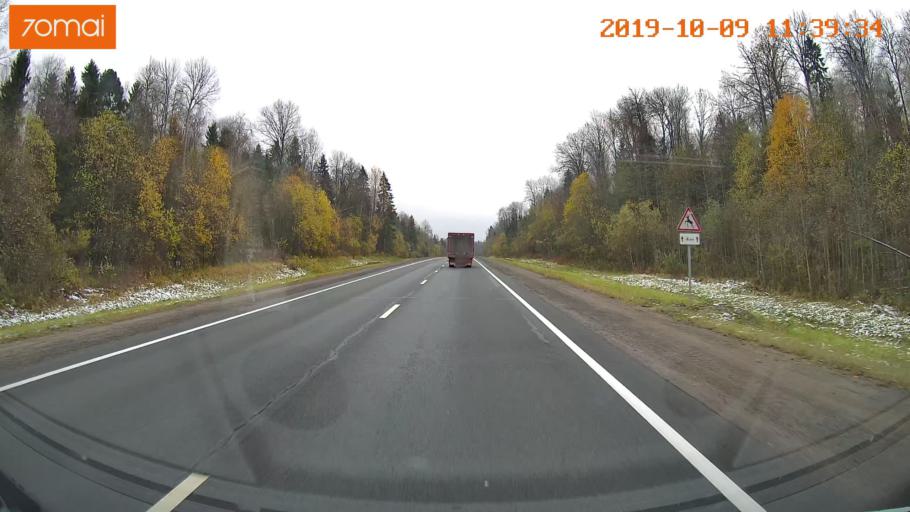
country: RU
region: Vologda
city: Gryazovets
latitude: 58.9545
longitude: 40.1672
